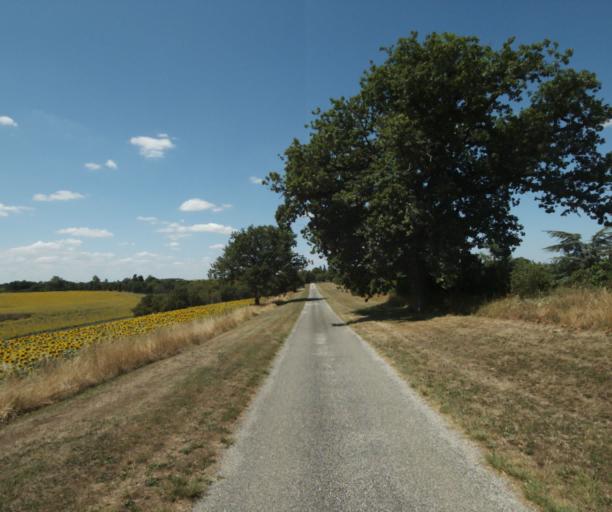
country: FR
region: Midi-Pyrenees
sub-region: Departement de la Haute-Garonne
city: Saint-Felix-Lauragais
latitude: 43.4761
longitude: 1.8634
